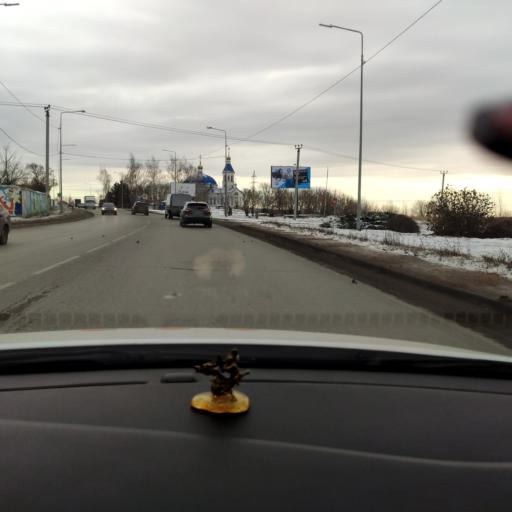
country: RU
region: Tatarstan
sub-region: Zelenodol'skiy Rayon
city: Zelenodolsk
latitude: 55.8467
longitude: 48.5495
